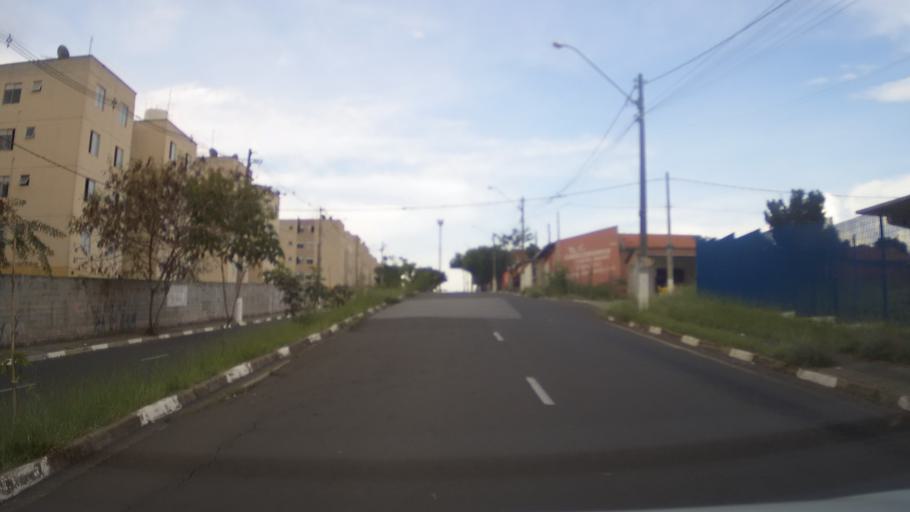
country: BR
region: Sao Paulo
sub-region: Hortolandia
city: Hortolandia
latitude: -22.9664
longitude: -47.2004
